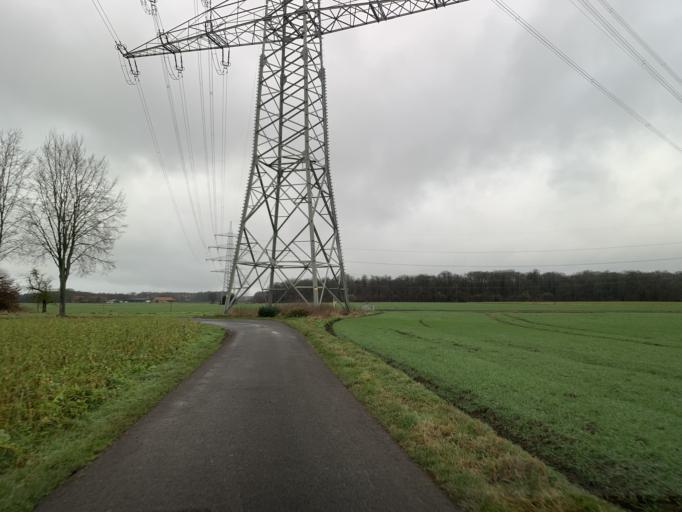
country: DE
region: North Rhine-Westphalia
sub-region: Regierungsbezirk Munster
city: Havixbeck
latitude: 51.9539
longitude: 7.4861
